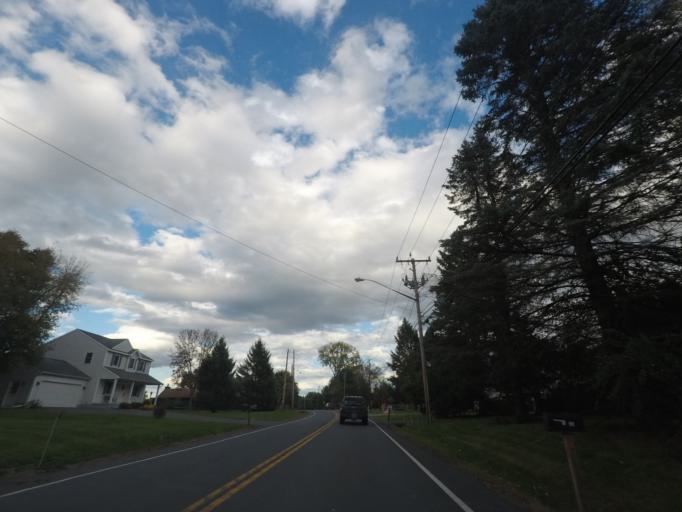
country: US
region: New York
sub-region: Rensselaer County
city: Hampton Manor
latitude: 42.6384
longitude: -73.7241
